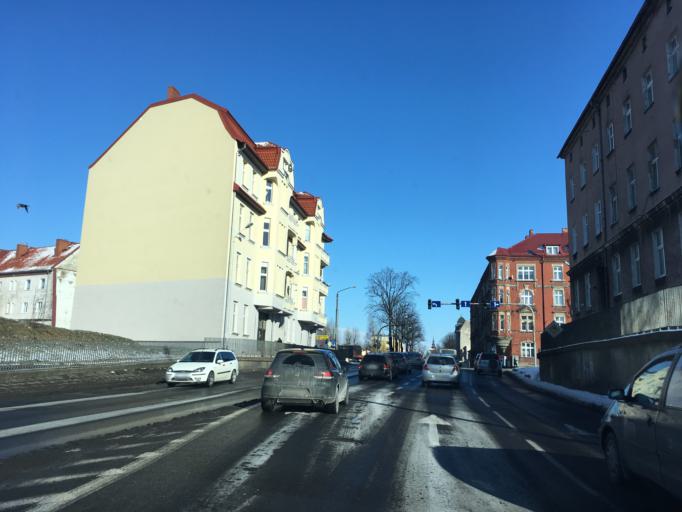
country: PL
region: Pomeranian Voivodeship
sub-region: Slupsk
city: Slupsk
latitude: 54.4637
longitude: 17.0163
